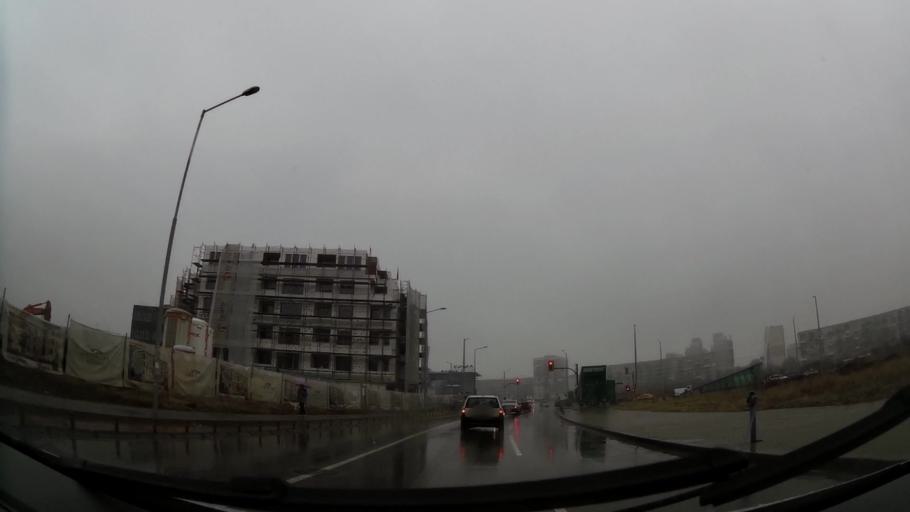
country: BG
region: Sofia-Capital
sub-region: Stolichna Obshtina
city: Sofia
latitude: 42.6568
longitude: 23.3941
